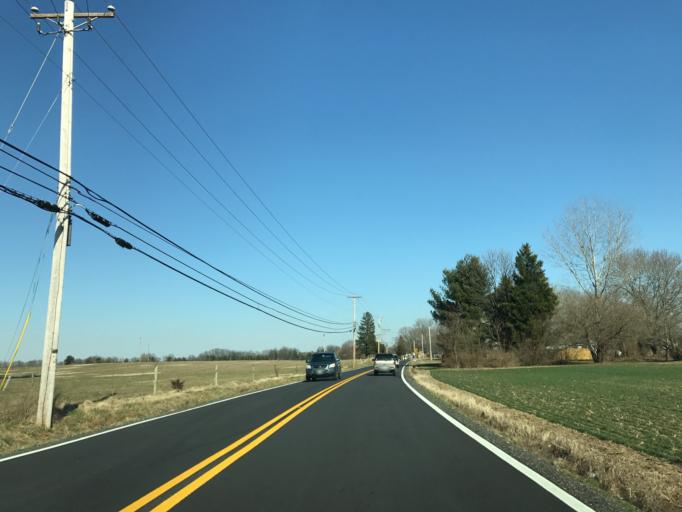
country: US
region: Maryland
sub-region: Queen Anne's County
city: Centreville
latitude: 39.0325
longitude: -76.0829
